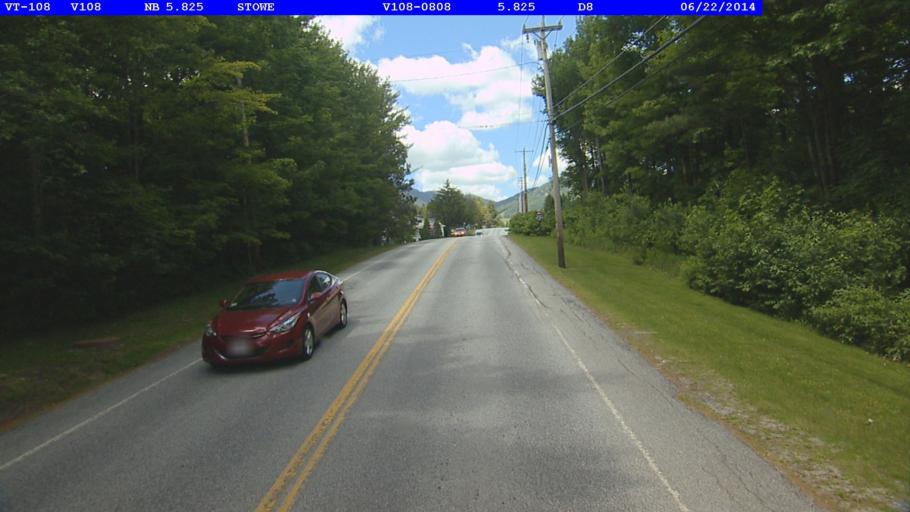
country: US
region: Vermont
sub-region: Lamoille County
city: Morristown
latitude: 44.5098
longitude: -72.7643
